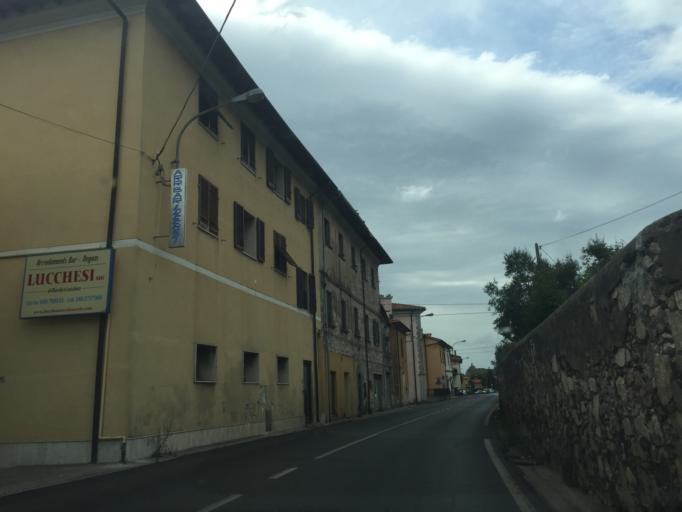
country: IT
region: Tuscany
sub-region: Province of Pisa
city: Uliveto Terme
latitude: 43.6936
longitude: 10.5212
